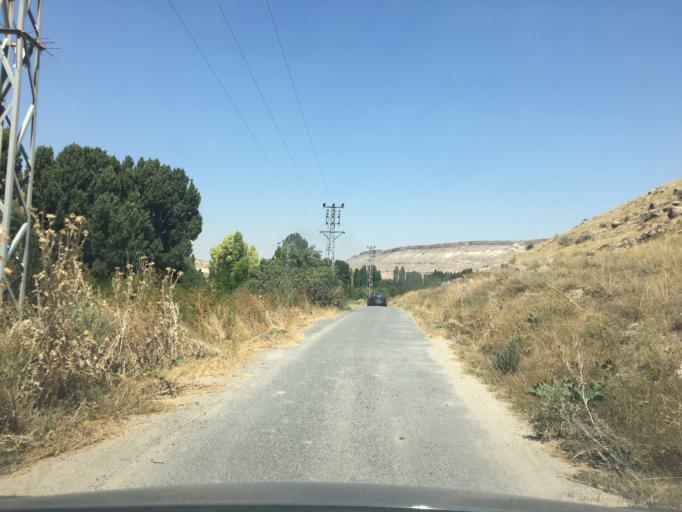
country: TR
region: Kayseri
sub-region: Yesilhisar
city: Yesilhisar
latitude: 38.4666
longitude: 34.9642
